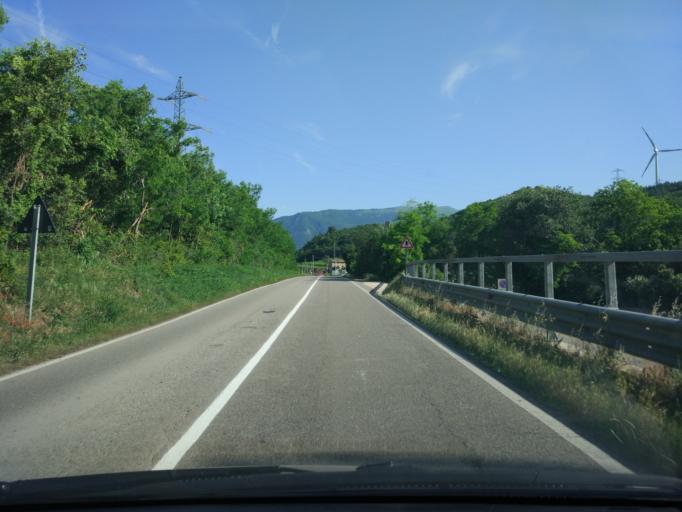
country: IT
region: Veneto
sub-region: Provincia di Verona
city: Affi
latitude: 45.5525
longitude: 10.8038
